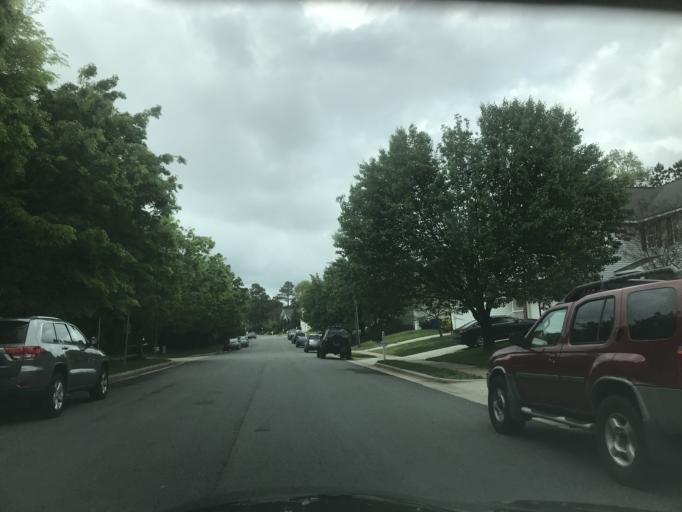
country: US
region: North Carolina
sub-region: Wake County
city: West Raleigh
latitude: 35.7449
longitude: -78.6837
